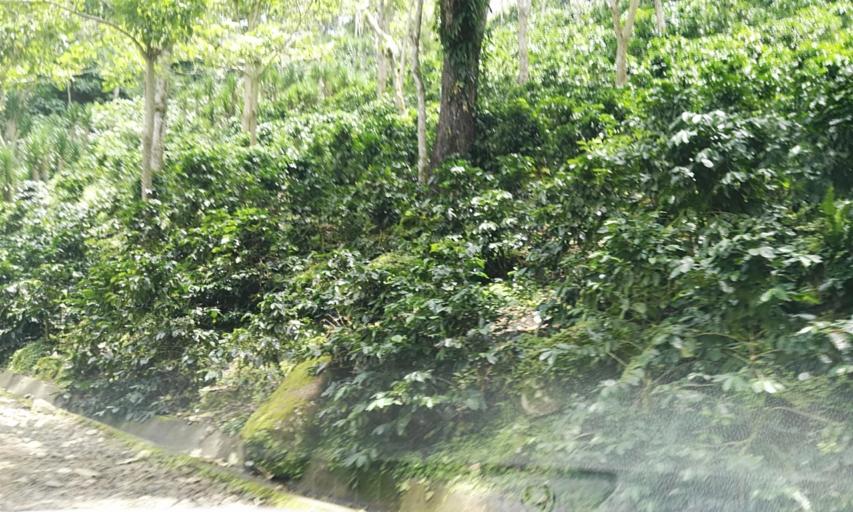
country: NI
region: Matagalpa
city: Matagalpa
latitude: 13.0173
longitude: -85.8818
